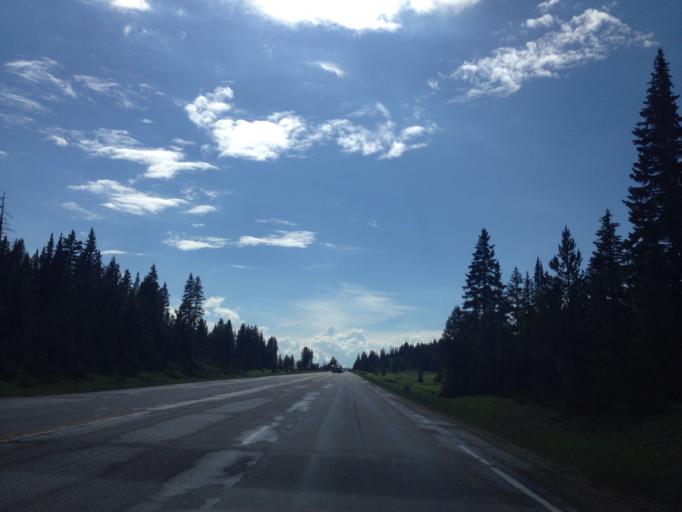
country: US
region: Colorado
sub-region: Routt County
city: Steamboat Springs
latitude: 40.3889
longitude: -106.6300
